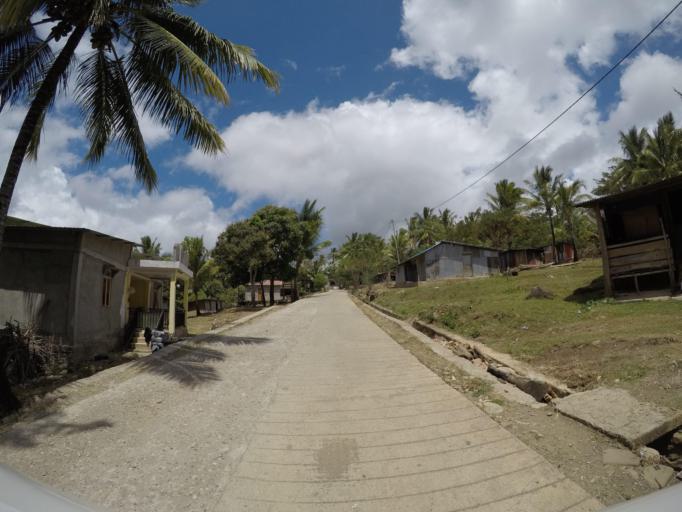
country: TL
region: Lautem
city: Lospalos
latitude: -8.5451
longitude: 126.8332
